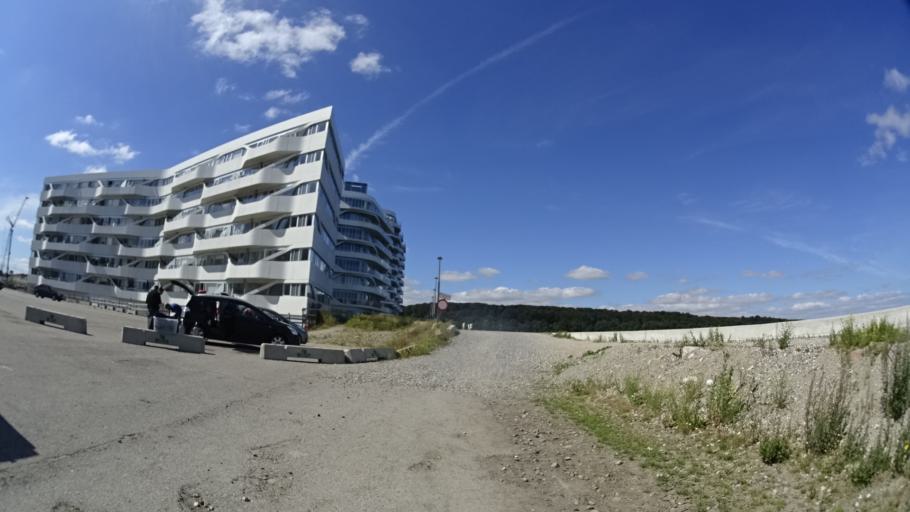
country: DK
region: Central Jutland
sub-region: Arhus Kommune
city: Arhus
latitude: 56.1661
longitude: 10.2314
